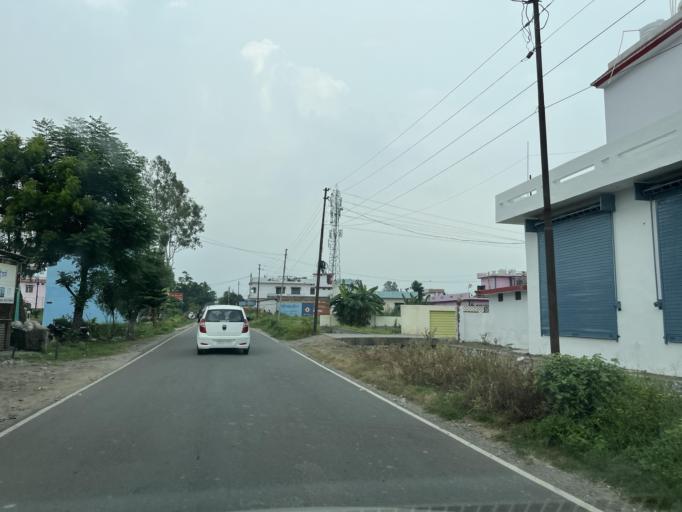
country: IN
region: Uttarakhand
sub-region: Naini Tal
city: Haldwani
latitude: 29.1943
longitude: 79.4837
